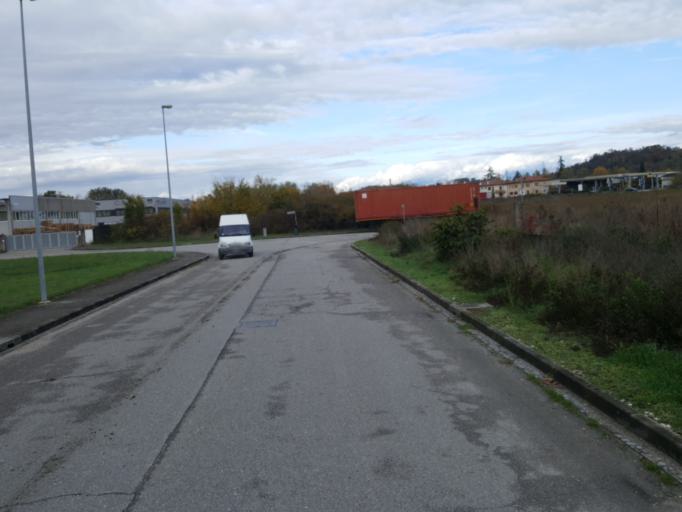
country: IT
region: Friuli Venezia Giulia
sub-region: Provincia di Udine
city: Manzano
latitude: 45.9880
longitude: 13.3655
